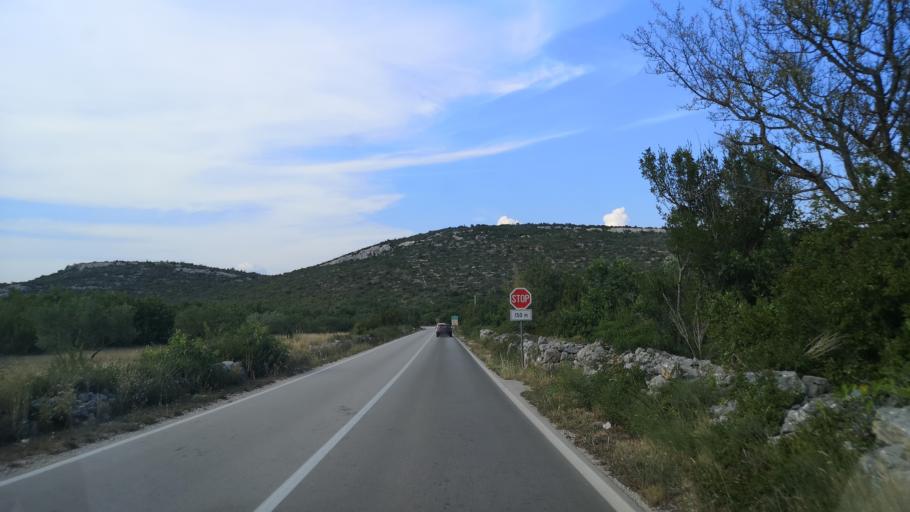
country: HR
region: Sibensko-Kniniska
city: Zaton
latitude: 43.8235
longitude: 15.7811
